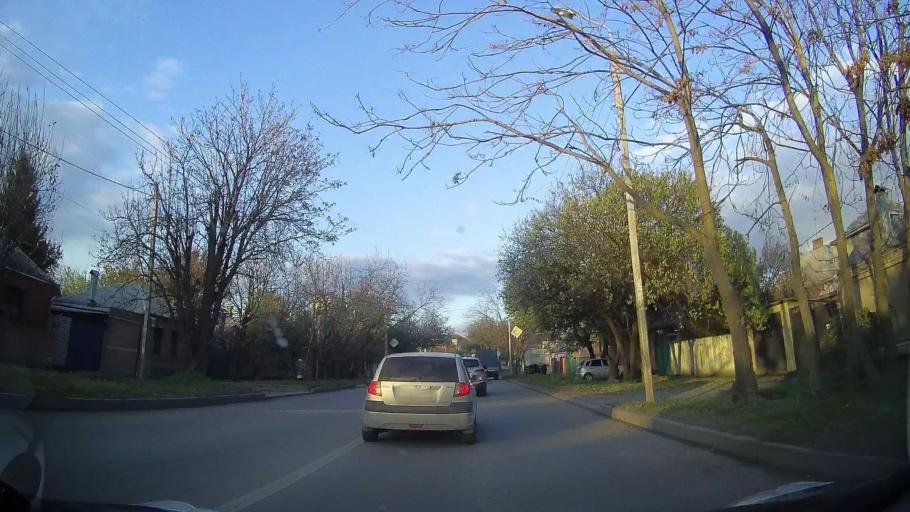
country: RU
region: Rostov
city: Imeni Chkalova
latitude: 47.2705
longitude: 39.7798
